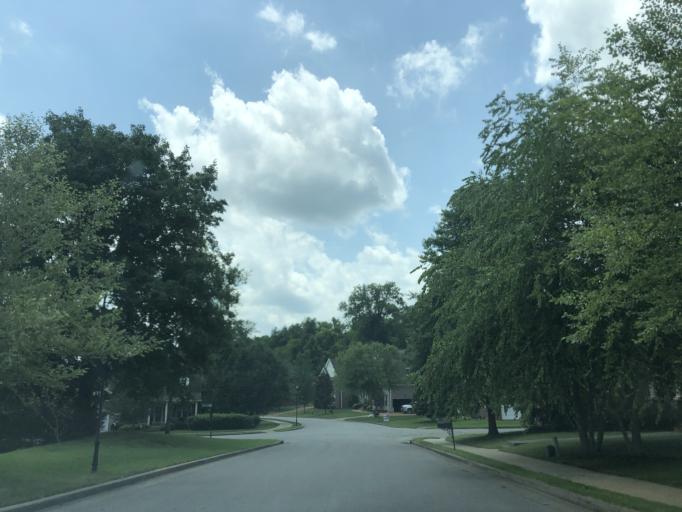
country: US
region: Tennessee
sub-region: Williamson County
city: Brentwood Estates
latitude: 36.0183
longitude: -86.7173
